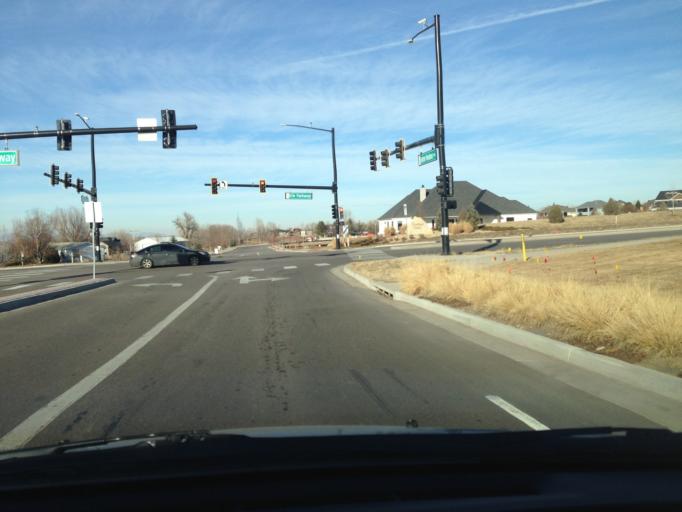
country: US
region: Colorado
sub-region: Boulder County
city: Erie
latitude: 40.0361
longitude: -105.0859
